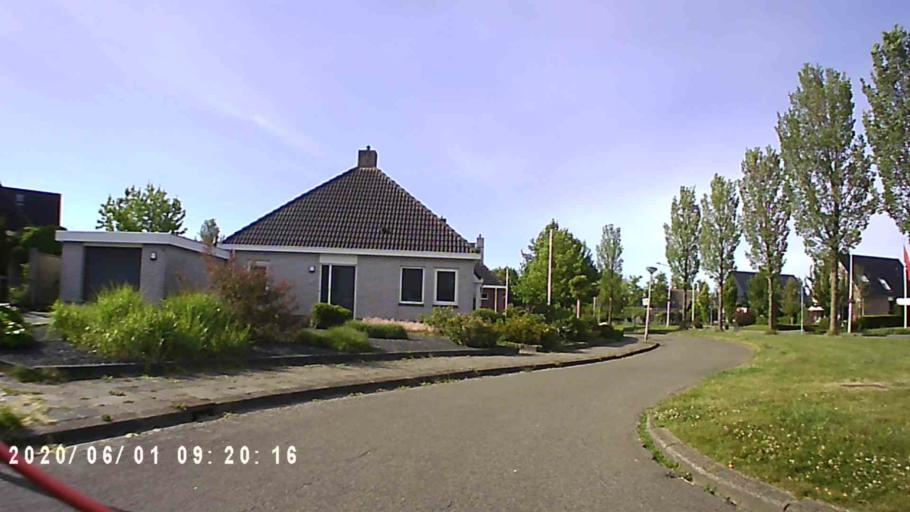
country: NL
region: Friesland
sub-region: Gemeente Leeuwarderadeel
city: Stiens
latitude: 53.2680
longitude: 5.7598
